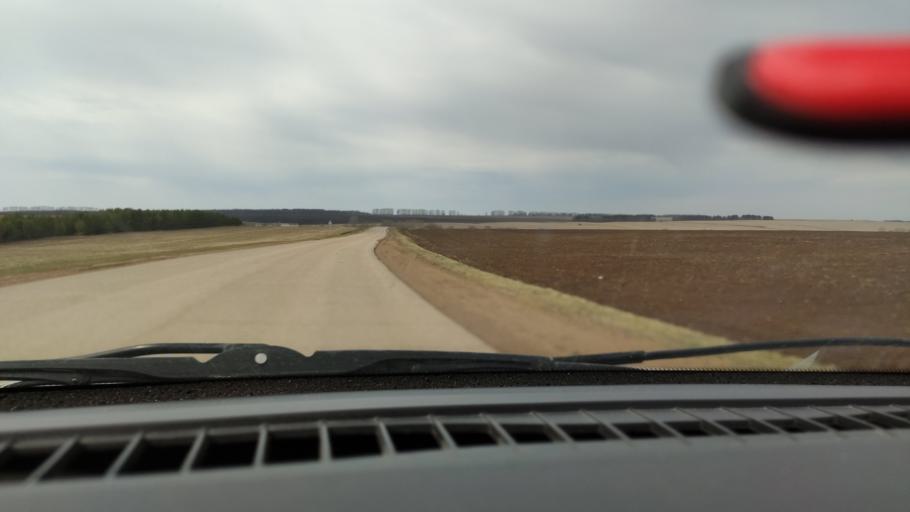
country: RU
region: Bashkortostan
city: Burayevo
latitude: 55.8030
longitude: 55.3559
